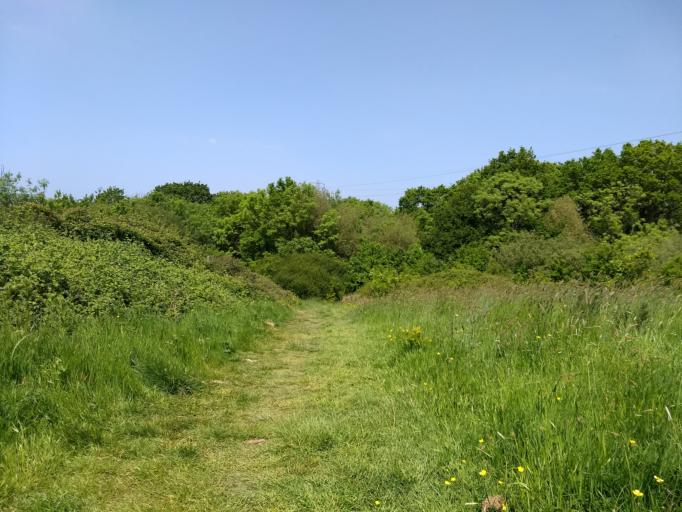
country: GB
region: England
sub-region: Isle of Wight
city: East Cowes
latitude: 50.7363
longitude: -1.2780
